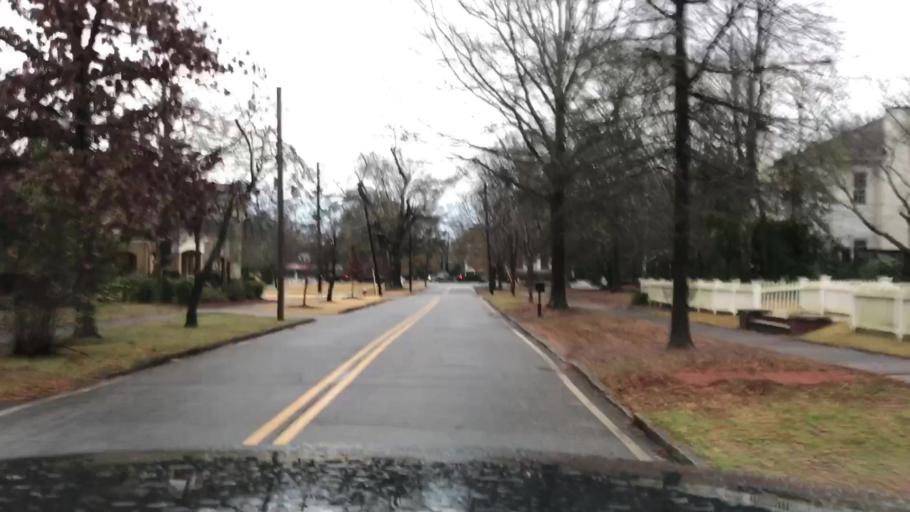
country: US
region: Georgia
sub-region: Morgan County
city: Madison
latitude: 33.5944
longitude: -83.4714
